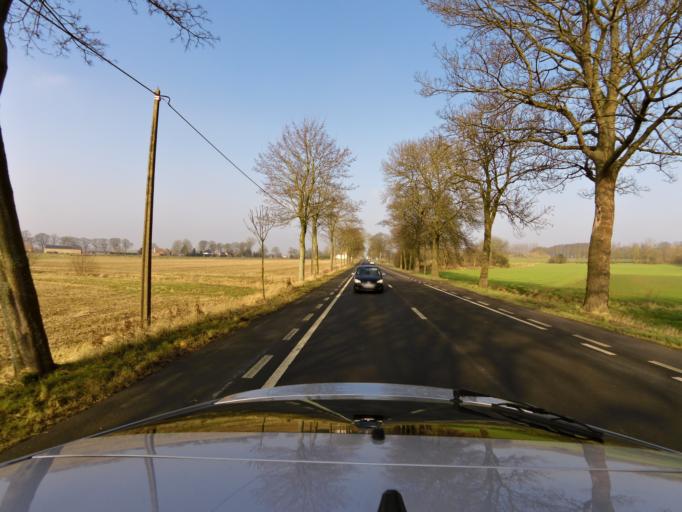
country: BE
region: Wallonia
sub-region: Province du Hainaut
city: Peruwelz
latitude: 50.5433
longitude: 3.6100
